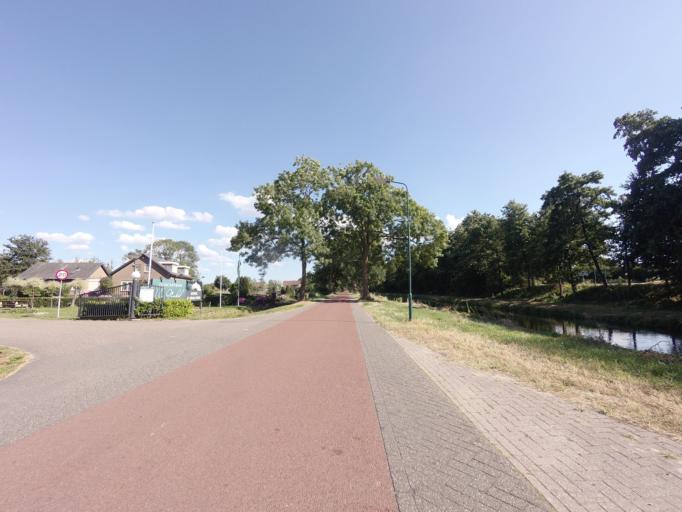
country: NL
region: Utrecht
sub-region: Stichtse Vecht
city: Maarssen
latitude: 52.1396
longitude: 5.0573
